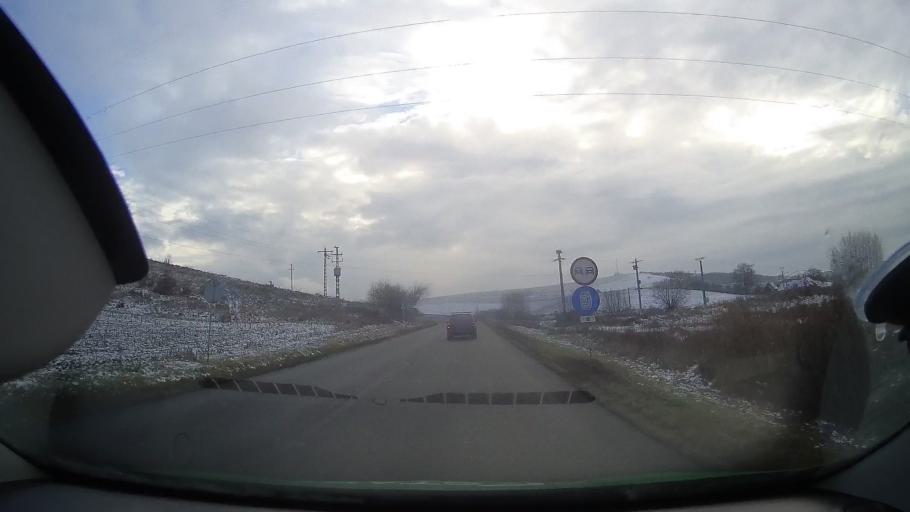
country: RO
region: Mures
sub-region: Comuna Cucerdea
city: Cucerdea
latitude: 46.4207
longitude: 24.2591
